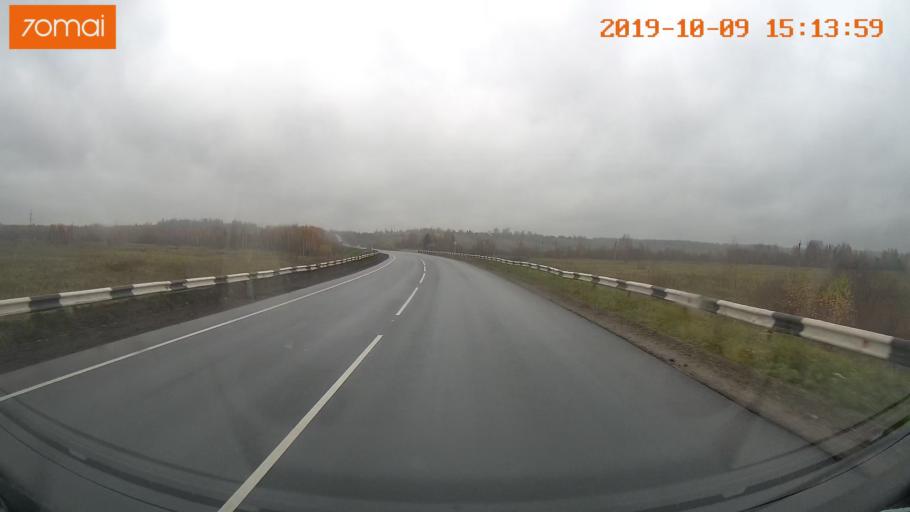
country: RU
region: Kostroma
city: Susanino
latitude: 58.1401
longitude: 41.6073
